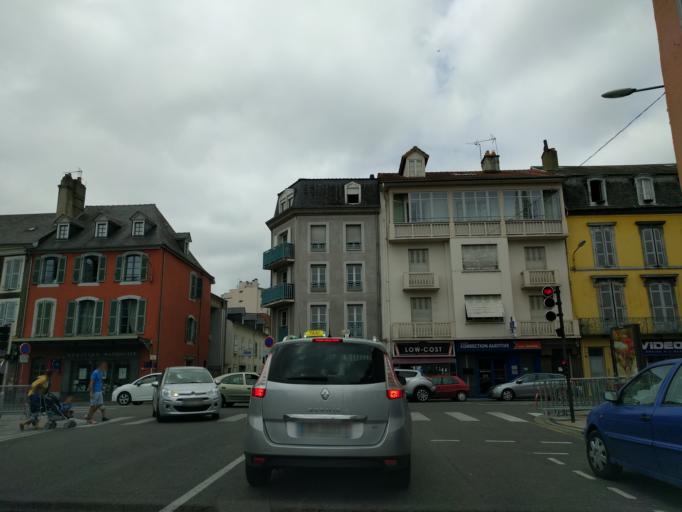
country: FR
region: Midi-Pyrenees
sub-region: Departement des Hautes-Pyrenees
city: Tarbes
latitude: 43.2314
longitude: 0.0821
